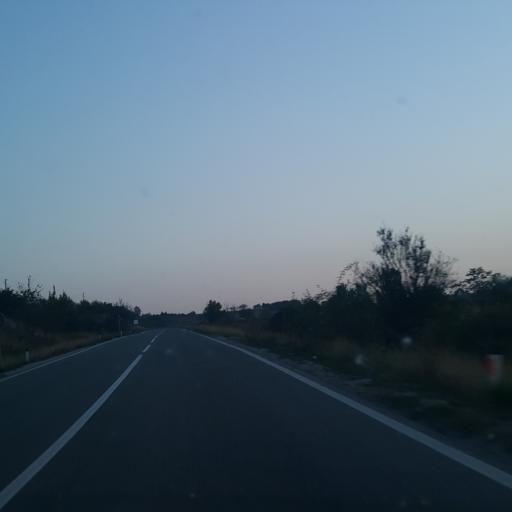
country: RS
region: Central Serbia
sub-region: Nisavski Okrug
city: Svrljig
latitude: 43.4332
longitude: 22.1613
